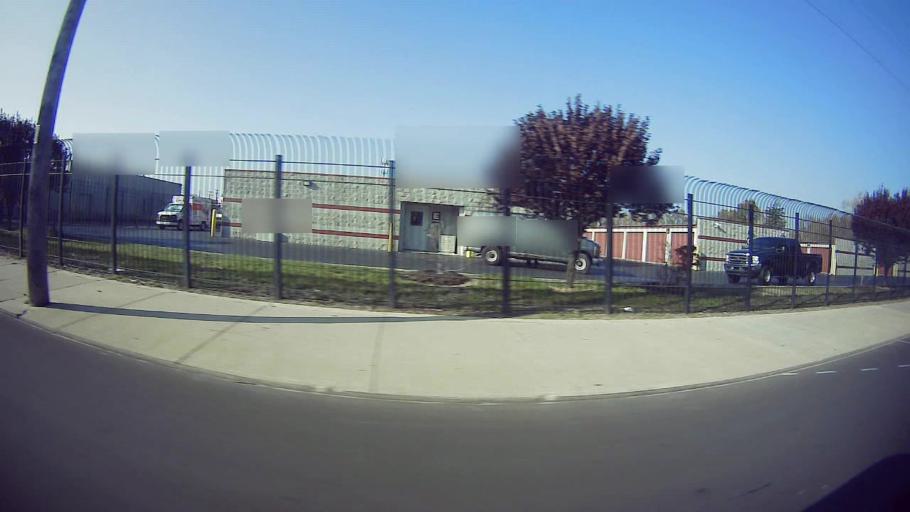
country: US
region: Michigan
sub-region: Oakland County
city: Oak Park
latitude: 42.3955
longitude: -83.1789
